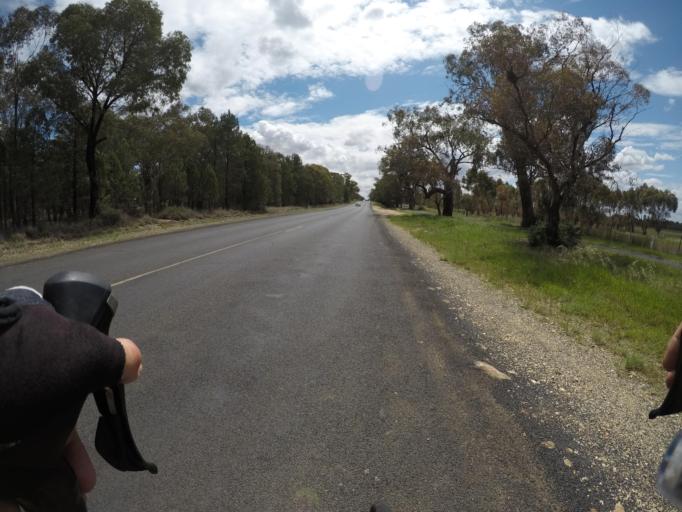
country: AU
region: New South Wales
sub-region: Dubbo Municipality
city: Dubbo
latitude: -32.2743
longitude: 148.5892
